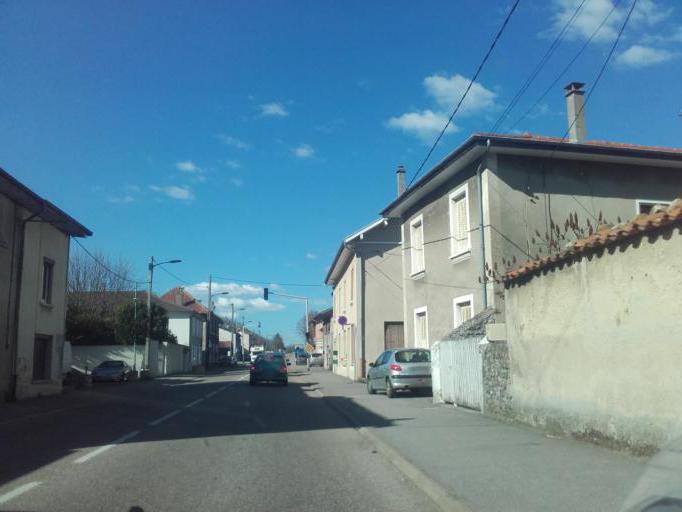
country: FR
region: Rhone-Alpes
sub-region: Departement de l'Isere
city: Champier
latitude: 45.4570
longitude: 5.2915
